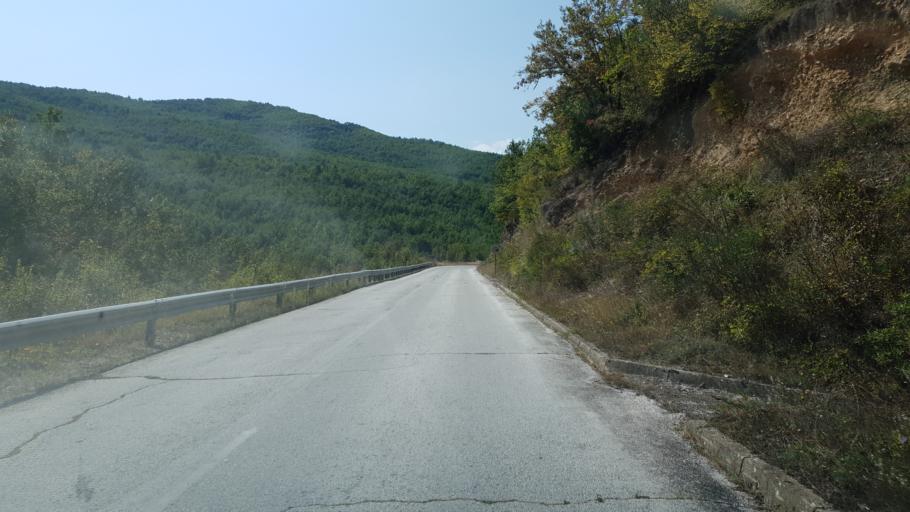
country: MK
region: Makedonski Brod
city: Samokov
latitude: 41.6658
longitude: 21.2309
